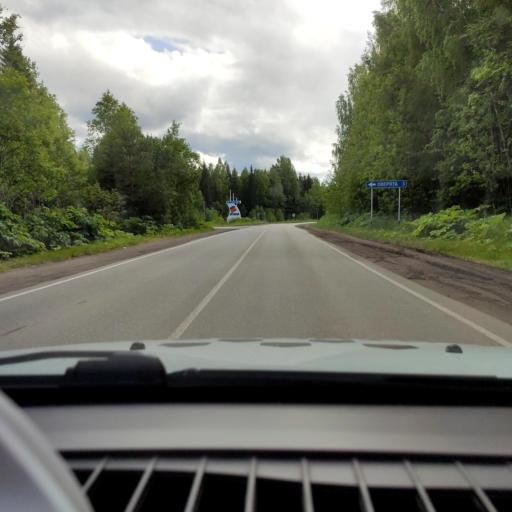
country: RU
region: Perm
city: Overyata
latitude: 58.1107
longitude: 55.8288
